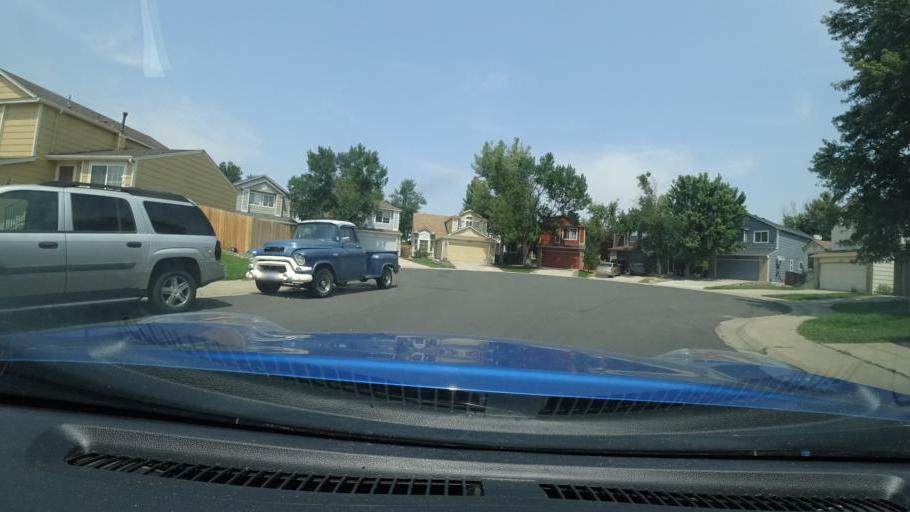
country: US
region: Colorado
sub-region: Adams County
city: Aurora
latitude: 39.7732
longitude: -104.7608
